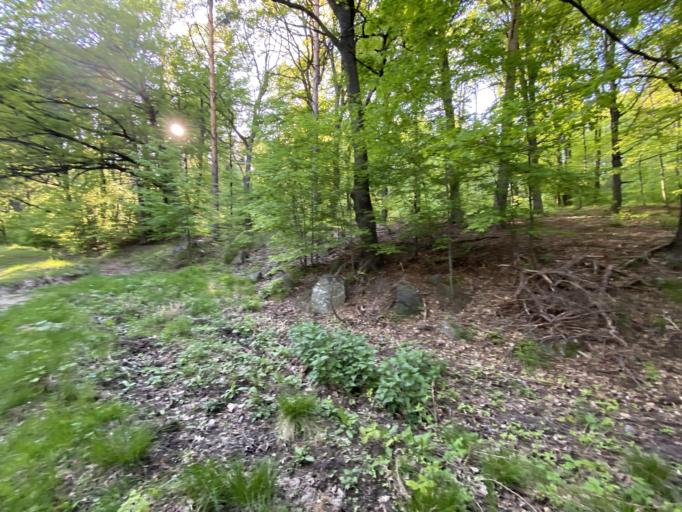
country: PL
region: Lower Silesian Voivodeship
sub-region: Powiat wroclawski
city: Sobotka
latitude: 50.8748
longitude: 16.7381
